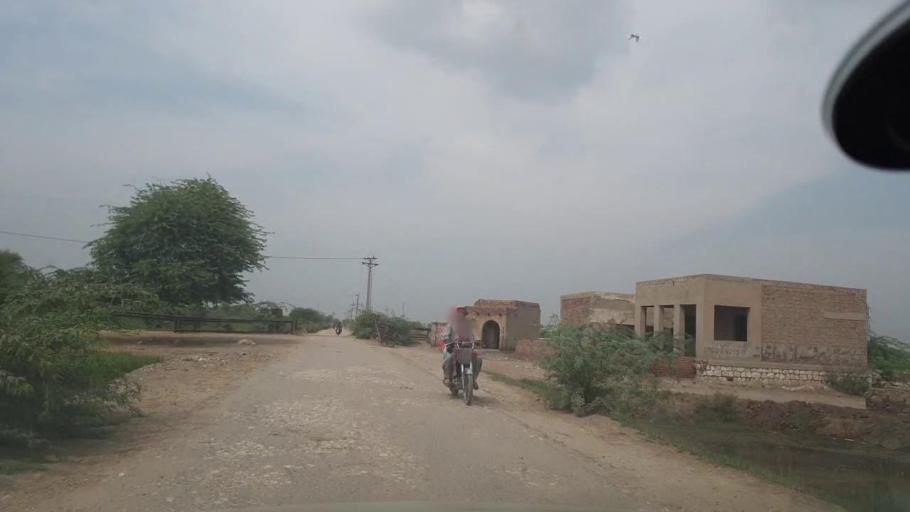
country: PK
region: Sindh
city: Jacobabad
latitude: 28.2589
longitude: 68.4373
